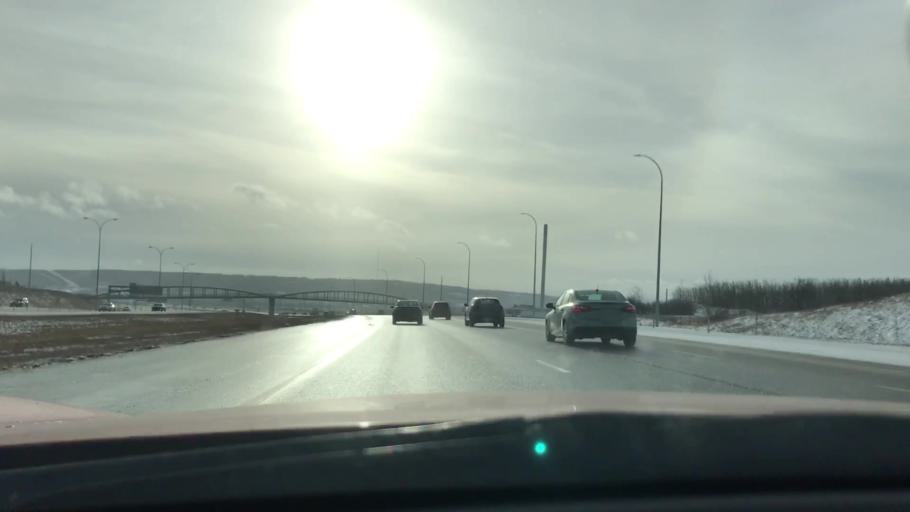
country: CA
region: Alberta
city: Calgary
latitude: 51.1286
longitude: -114.2303
